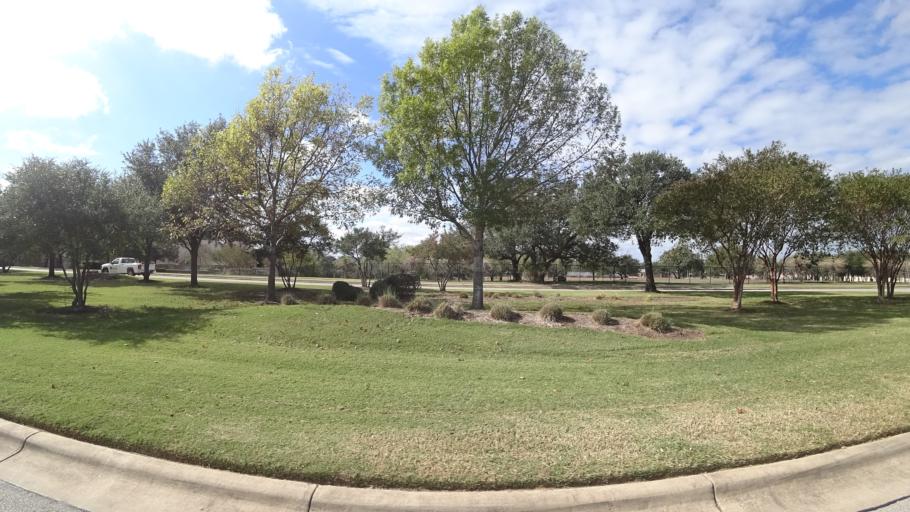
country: US
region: Texas
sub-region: Travis County
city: Hudson Bend
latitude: 30.3637
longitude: -97.9006
